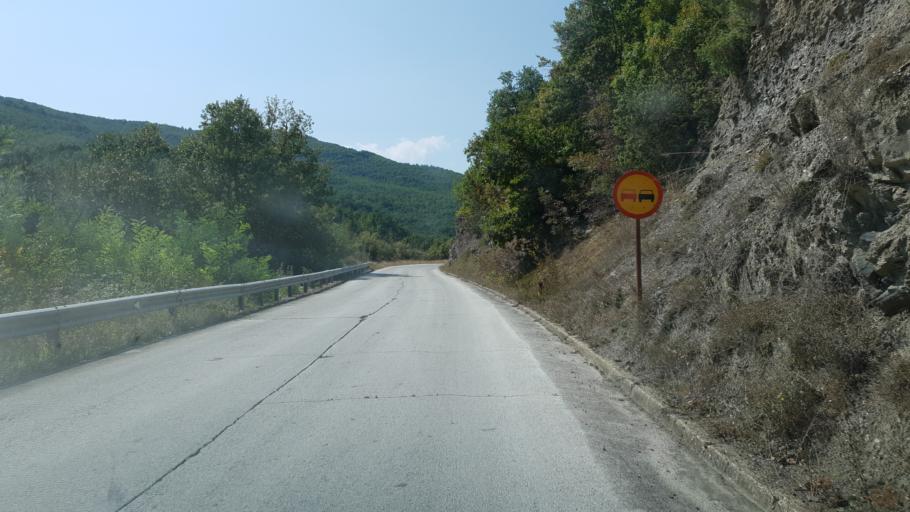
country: MK
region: Makedonski Brod
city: Samokov
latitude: 41.6681
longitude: 21.2344
